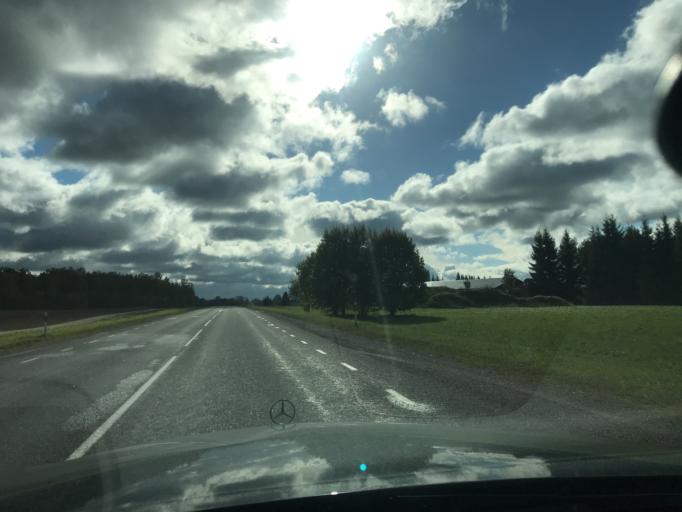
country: EE
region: Vorumaa
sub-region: Antsla vald
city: Vana-Antsla
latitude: 57.9356
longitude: 26.3135
